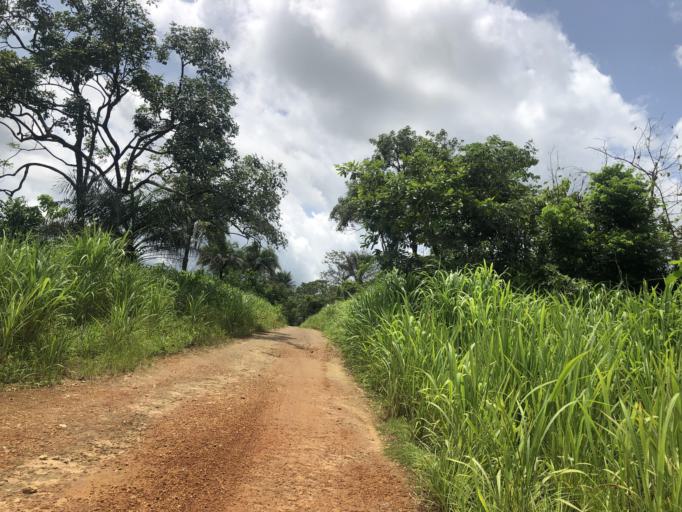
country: SL
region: Northern Province
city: Bumbuna
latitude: 9.0022
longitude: -11.7657
